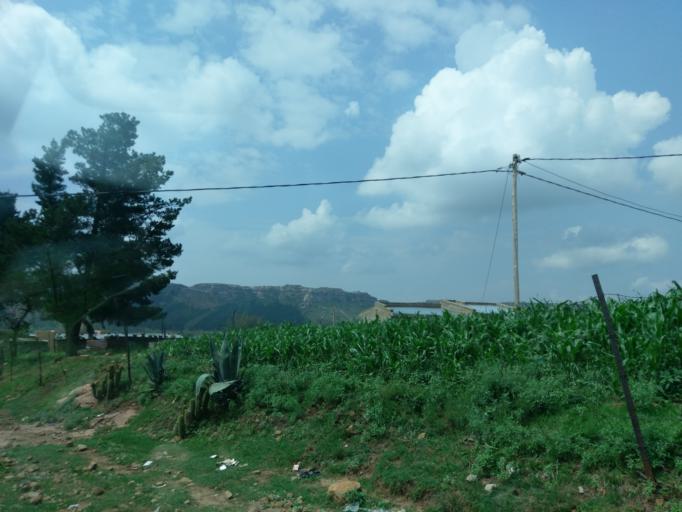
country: LS
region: Leribe
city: Leribe
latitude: -29.0230
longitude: 28.0166
